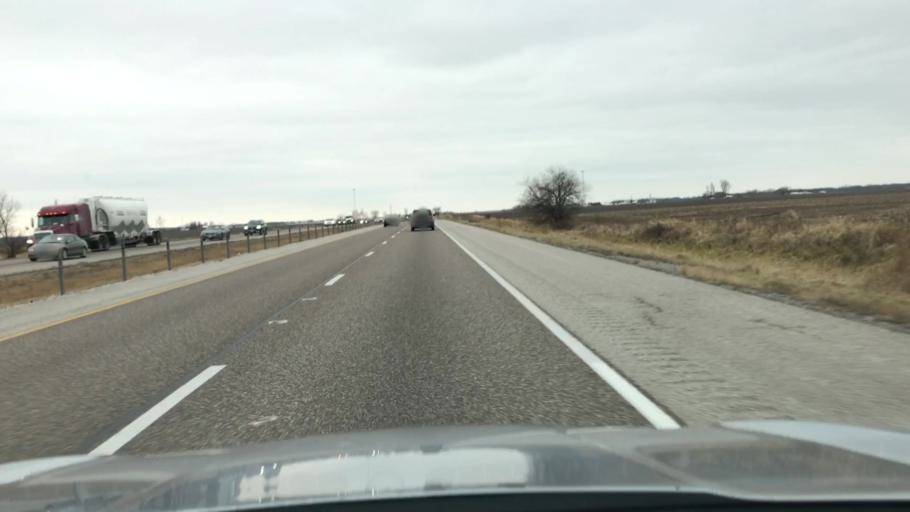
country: US
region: Illinois
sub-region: Madison County
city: Worden
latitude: 38.8476
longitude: -89.8674
